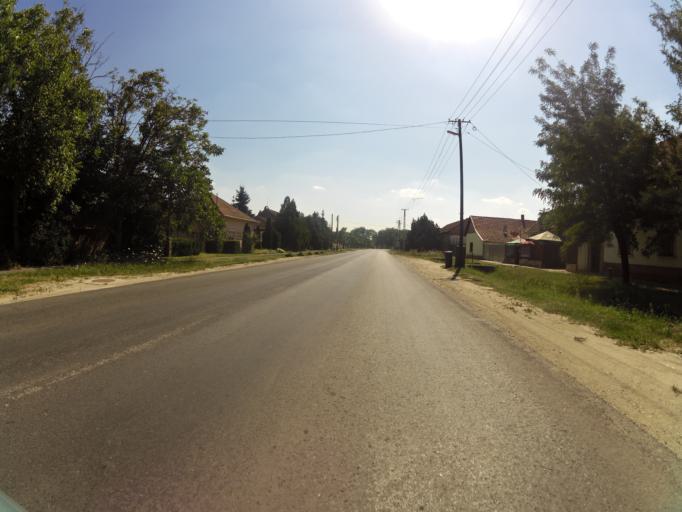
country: HU
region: Csongrad
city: Sandorfalva
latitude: 46.3598
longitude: 20.0939
